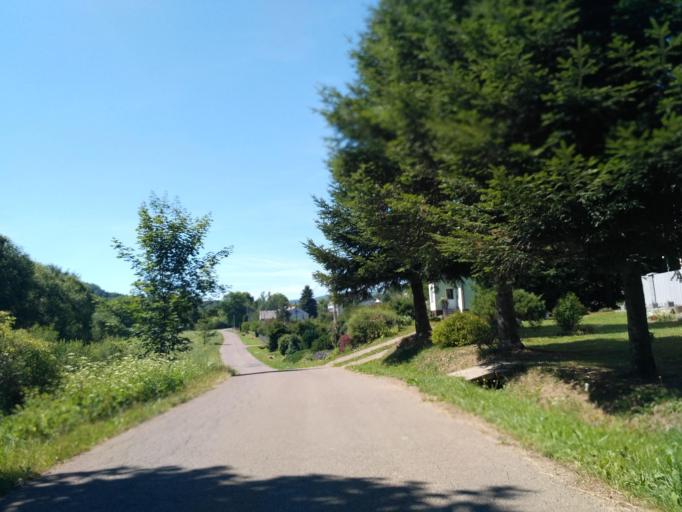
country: PL
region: Subcarpathian Voivodeship
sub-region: Powiat sanocki
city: Nowosielce-Gniewosz
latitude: 49.5299
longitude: 22.0449
